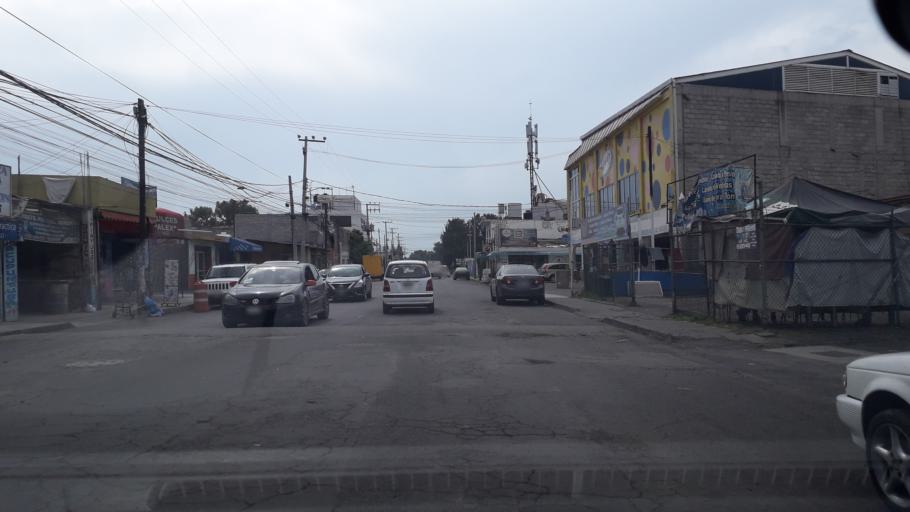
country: MX
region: Mexico
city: Ecatepec
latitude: 19.6373
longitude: -99.0773
